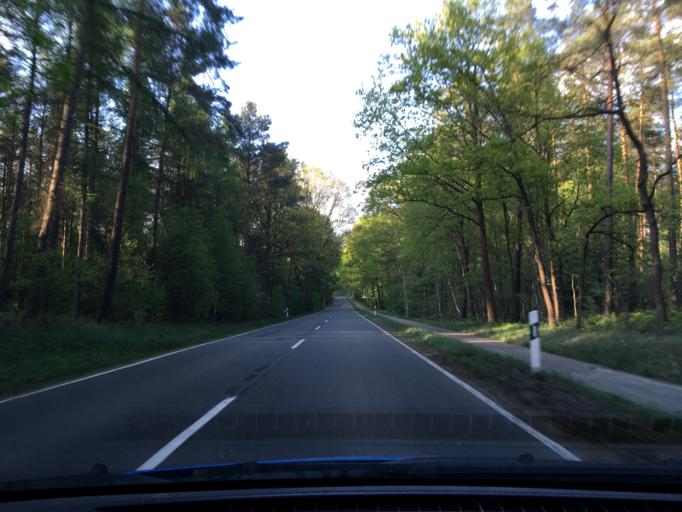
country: DE
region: Lower Saxony
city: Winsen
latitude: 52.7110
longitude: 9.9192
